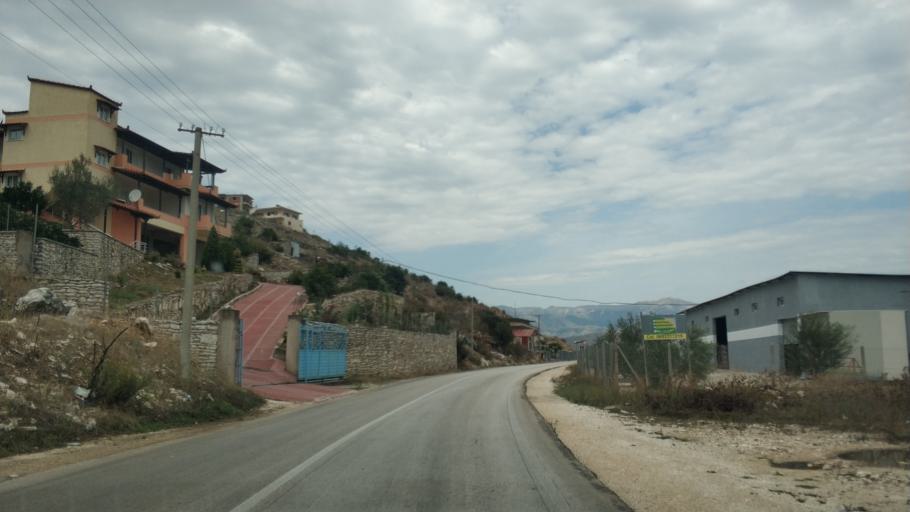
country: AL
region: Vlore
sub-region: Rrethi i Sarandes
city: Sarande
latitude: 39.8511
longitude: 20.0351
